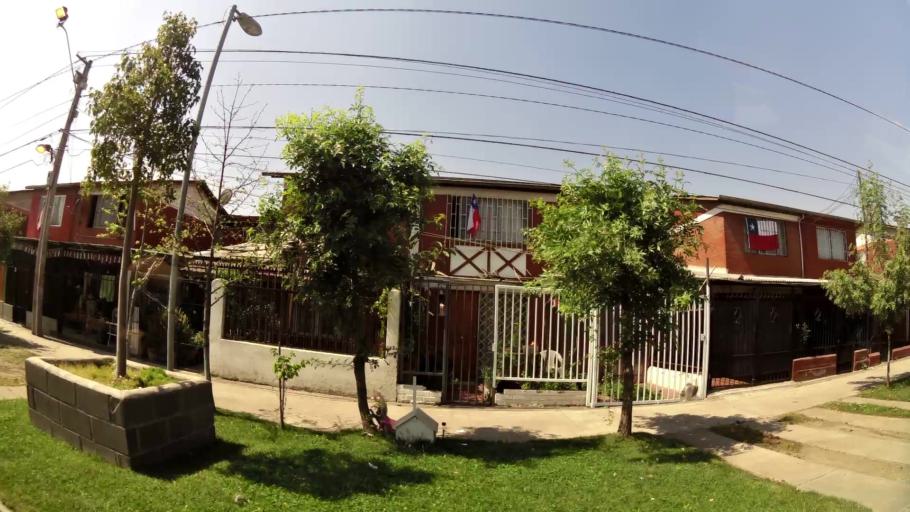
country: CL
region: Santiago Metropolitan
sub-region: Provincia de Santiago
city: La Pintana
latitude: -33.5474
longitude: -70.6184
